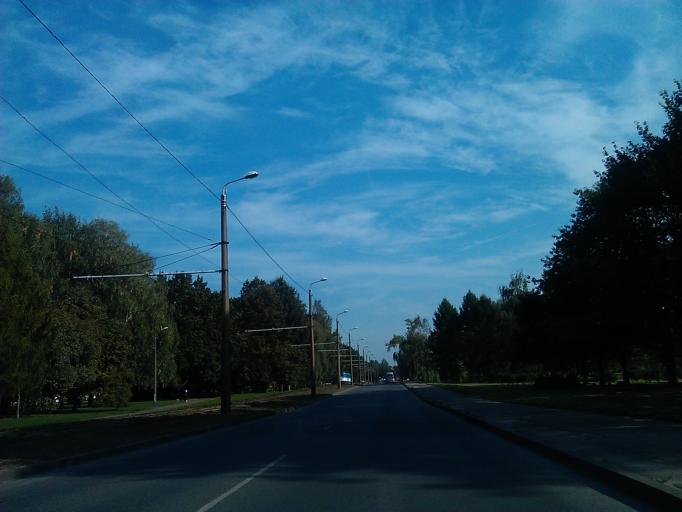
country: LV
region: Riga
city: Riga
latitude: 56.9414
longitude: 24.0842
